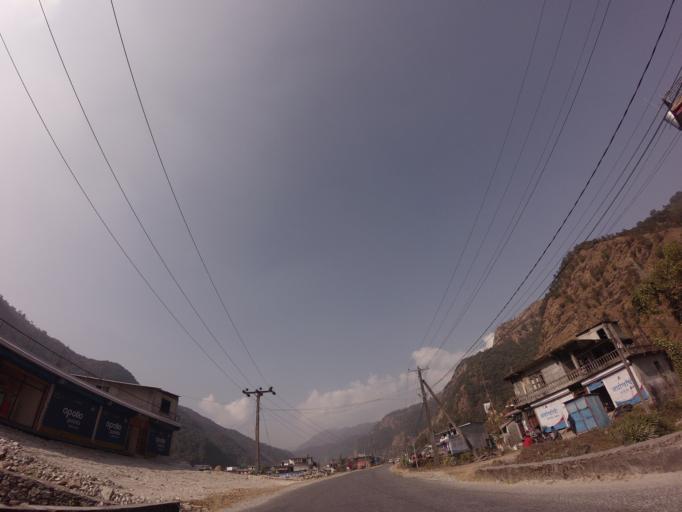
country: NP
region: Western Region
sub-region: Gandaki Zone
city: Pokhara
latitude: 28.2857
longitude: 83.9022
